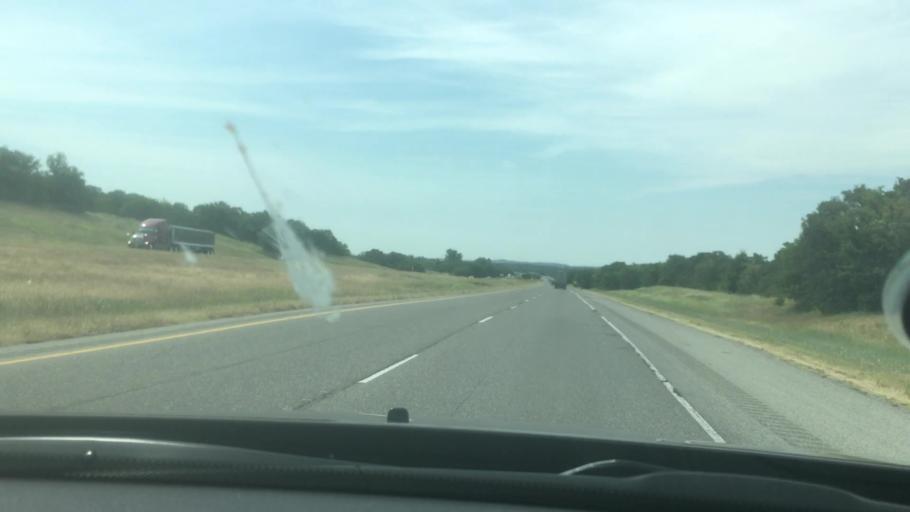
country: US
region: Oklahoma
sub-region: Murray County
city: Davis
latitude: 34.5411
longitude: -97.1896
